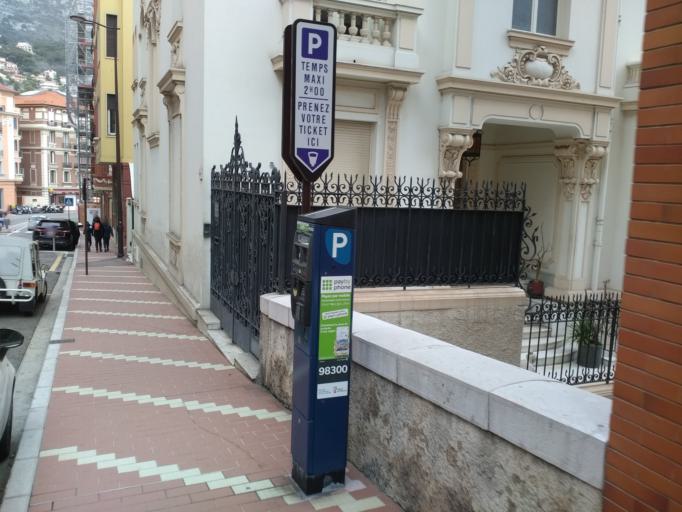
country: MC
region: Commune de Monaco
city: Moneghetti
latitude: 43.7359
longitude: 7.4164
